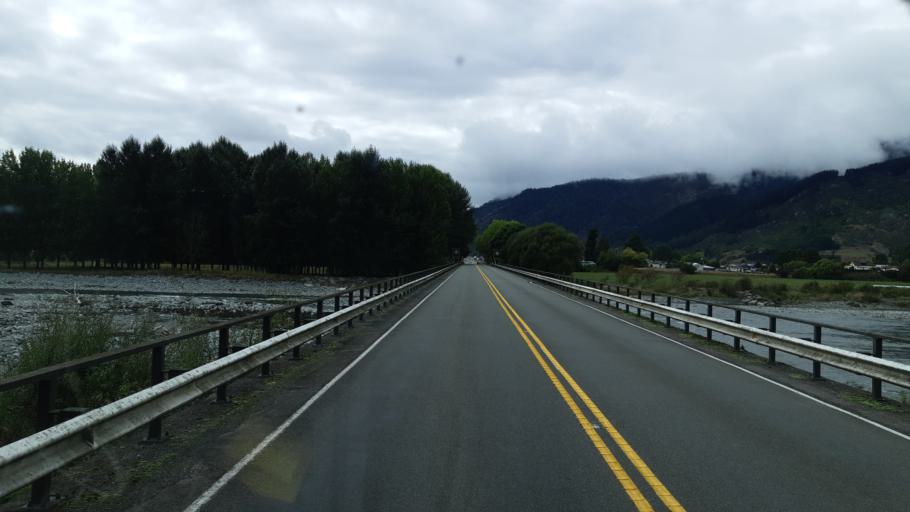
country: NZ
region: West Coast
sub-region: Buller District
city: Westport
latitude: -41.8000
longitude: 172.3174
